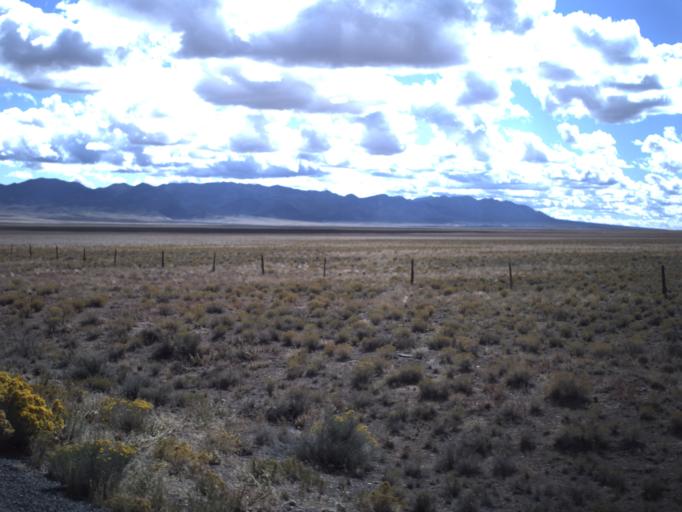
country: US
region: Utah
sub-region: Beaver County
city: Milford
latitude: 38.5543
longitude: -113.7415
